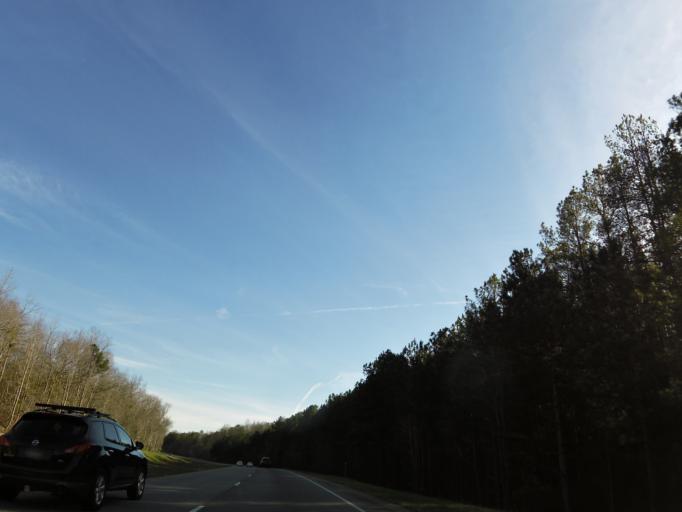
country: US
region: Georgia
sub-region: Chattahoochee County
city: Cusseta
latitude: 32.2454
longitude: -84.7193
